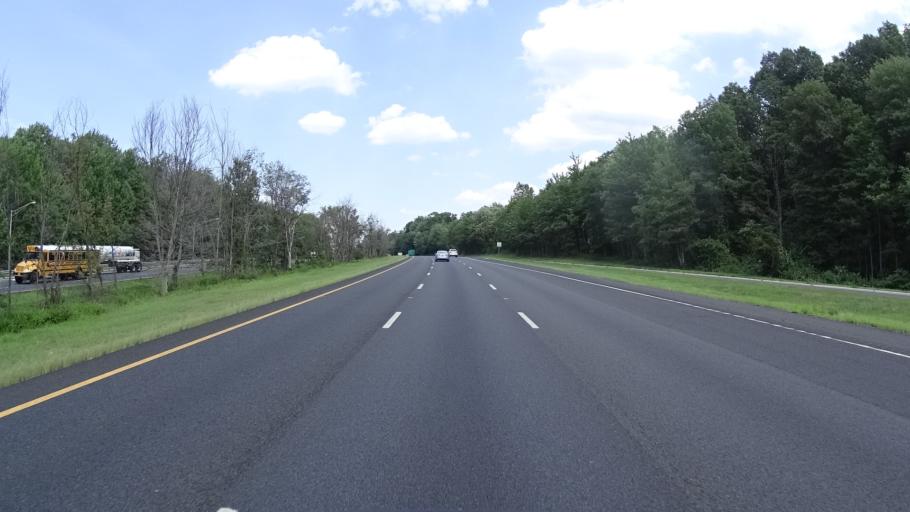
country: US
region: New Jersey
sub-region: Somerset County
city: Watchung
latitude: 40.6520
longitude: -74.4523
